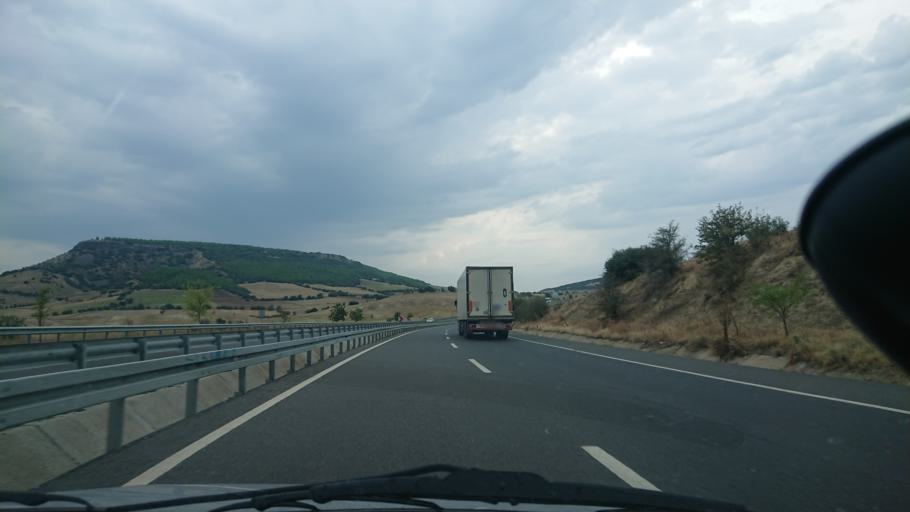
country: TR
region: Manisa
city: Selendi
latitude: 38.6168
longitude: 28.8761
